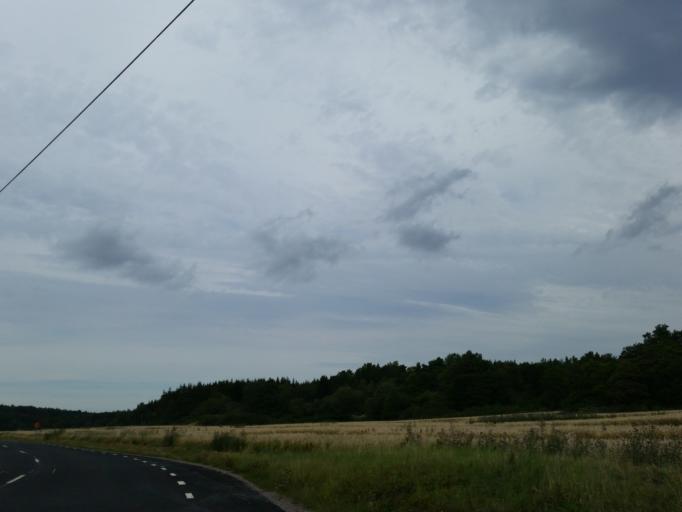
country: SE
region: Soedermanland
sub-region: Strangnas Kommun
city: Mariefred
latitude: 59.2550
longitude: 17.1807
